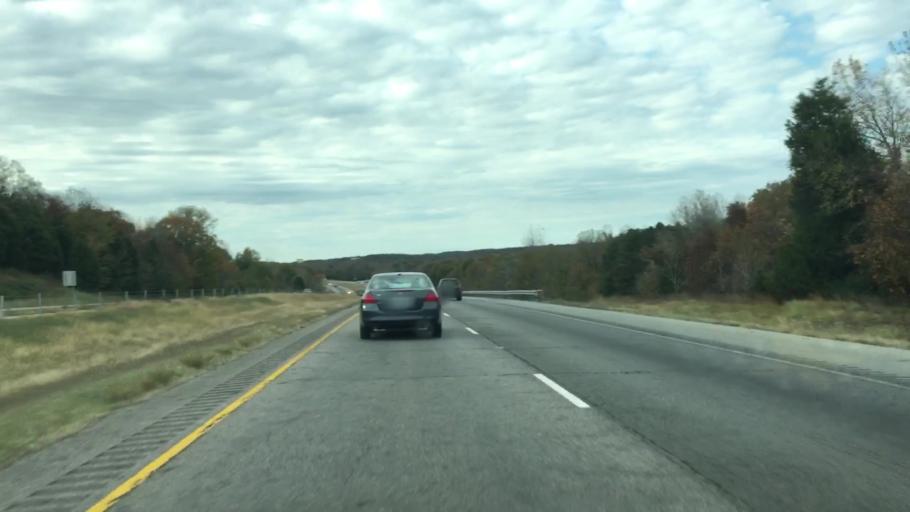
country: US
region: Arkansas
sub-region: Faulkner County
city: Conway
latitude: 35.1482
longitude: -92.5412
